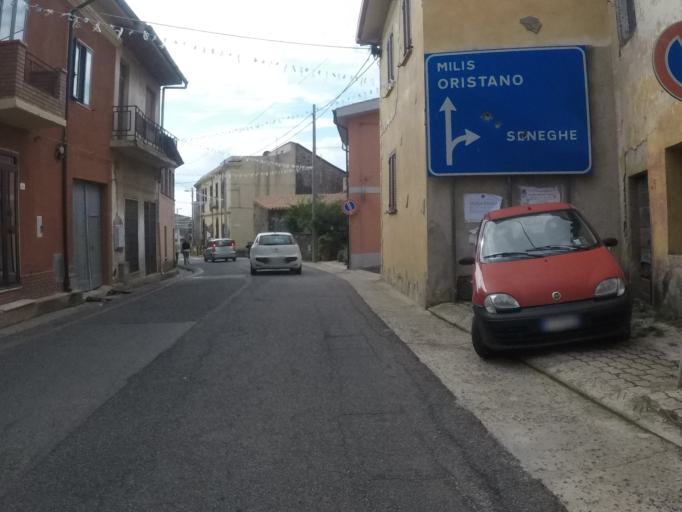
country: IT
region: Sardinia
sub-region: Provincia di Oristano
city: Bonarcado
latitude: 40.0980
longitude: 8.6549
